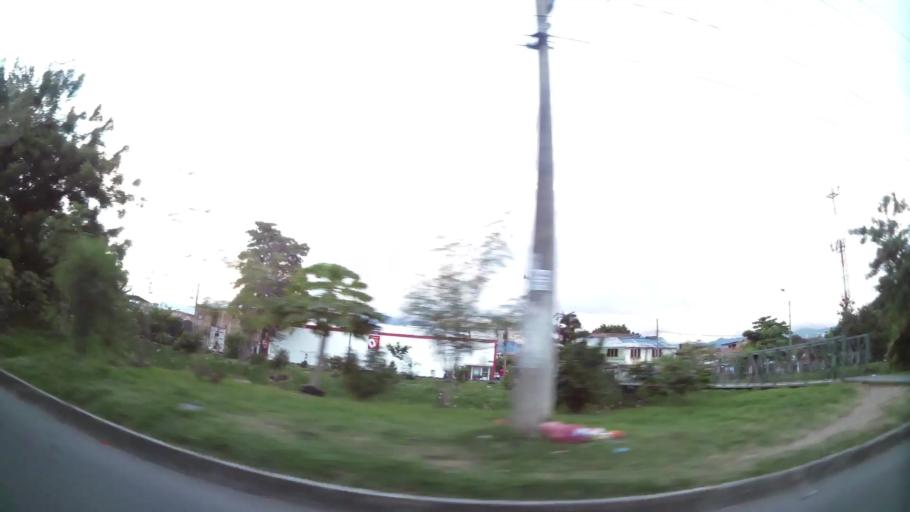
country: CO
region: Valle del Cauca
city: Cali
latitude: 3.4325
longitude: -76.4837
